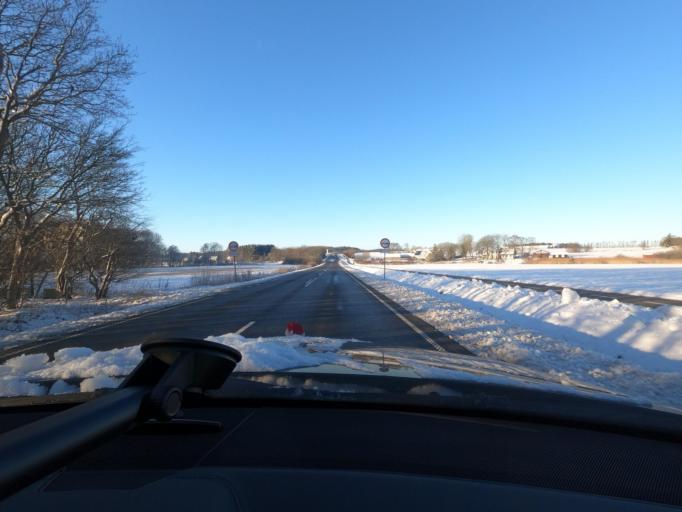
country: DK
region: South Denmark
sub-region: Tonder Kommune
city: Toftlund
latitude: 55.1339
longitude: 9.1324
